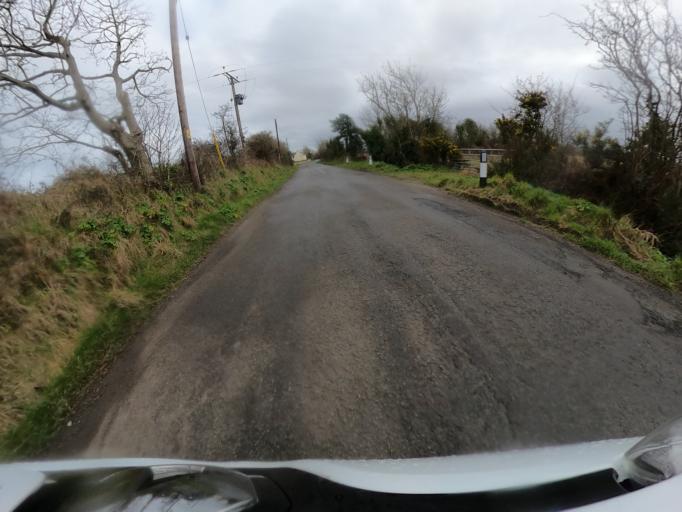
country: IM
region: Ramsey
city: Ramsey
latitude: 54.3766
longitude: -4.4467
